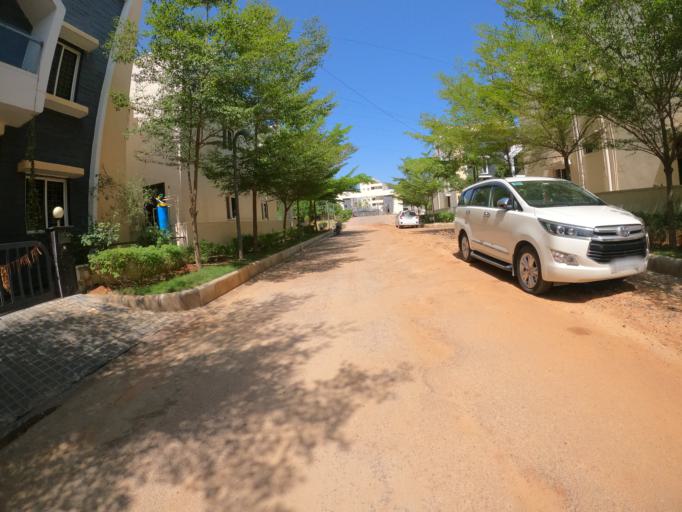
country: IN
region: Telangana
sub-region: Hyderabad
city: Hyderabad
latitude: 17.3597
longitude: 78.3809
